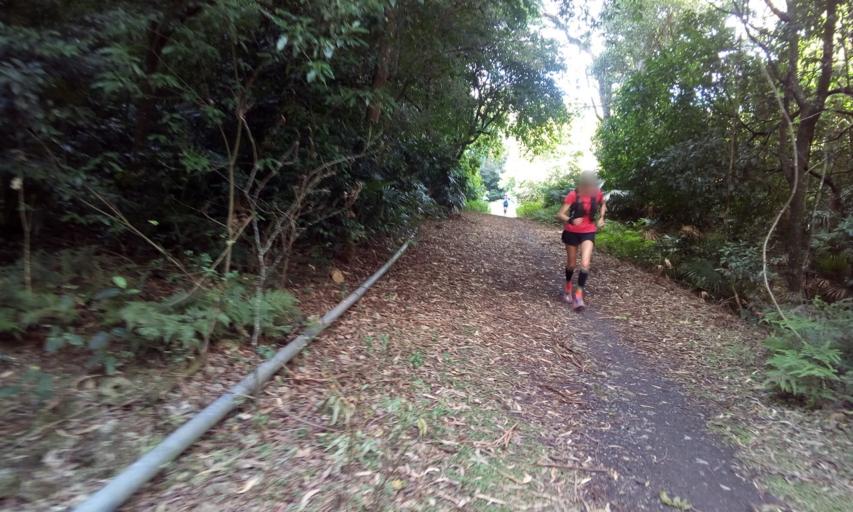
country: AU
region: New South Wales
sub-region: Wollongong
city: Cordeaux Heights
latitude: -34.4420
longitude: 150.8123
